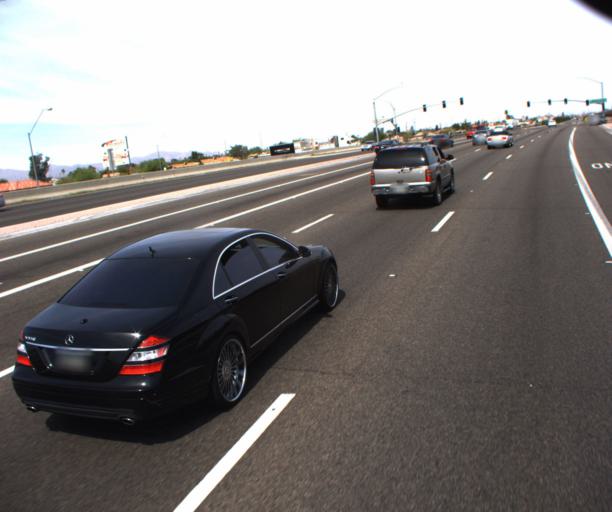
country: US
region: Arizona
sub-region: Maricopa County
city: El Mirage
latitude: 33.6097
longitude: -112.3129
